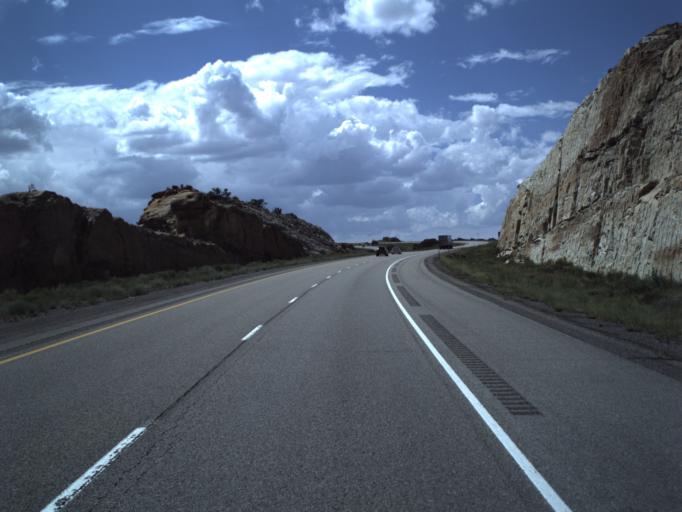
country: US
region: Utah
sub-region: Emery County
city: Ferron
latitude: 38.8652
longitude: -110.7961
